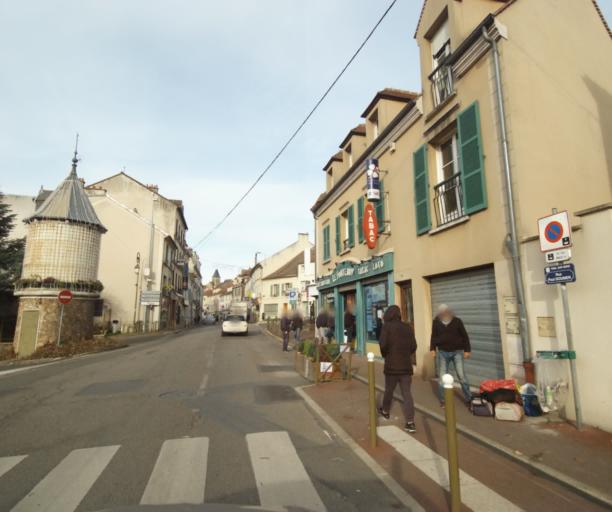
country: FR
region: Ile-de-France
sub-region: Departement des Yvelines
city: Triel-sur-Seine
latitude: 48.9797
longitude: 2.0040
